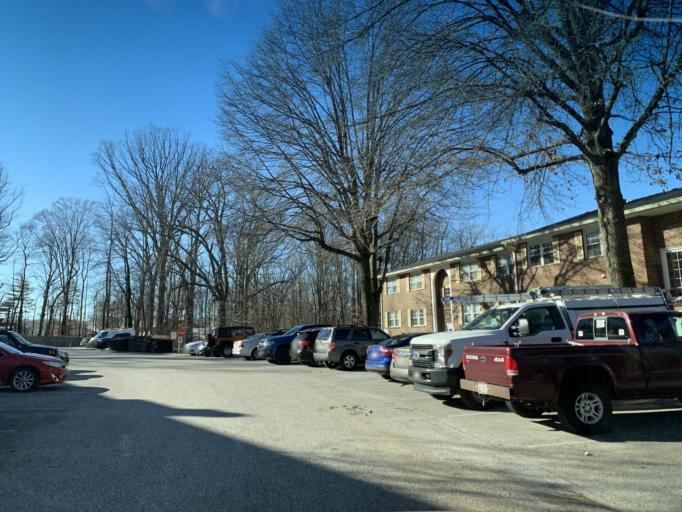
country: US
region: Maryland
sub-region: Harford County
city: North Bel Air
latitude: 39.5451
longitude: -76.3527
